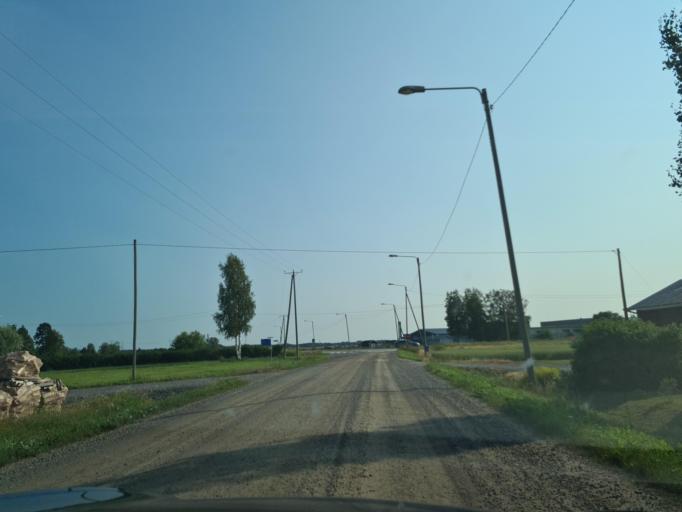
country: FI
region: Ostrobothnia
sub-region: Kyroenmaa
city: Laihia
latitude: 63.0019
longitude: 21.9025
